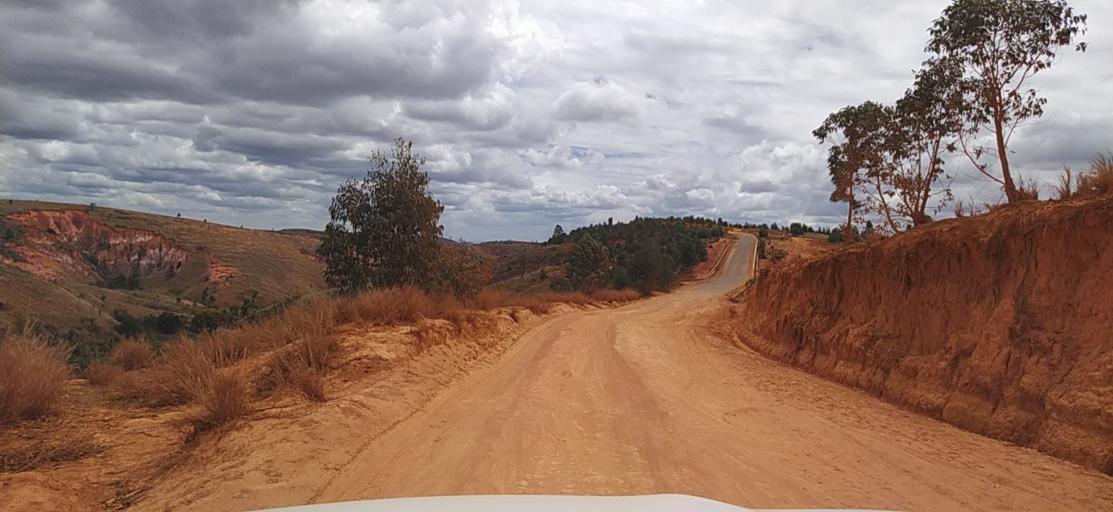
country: MG
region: Alaotra Mangoro
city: Ambatondrazaka
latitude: -18.0592
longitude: 48.2562
